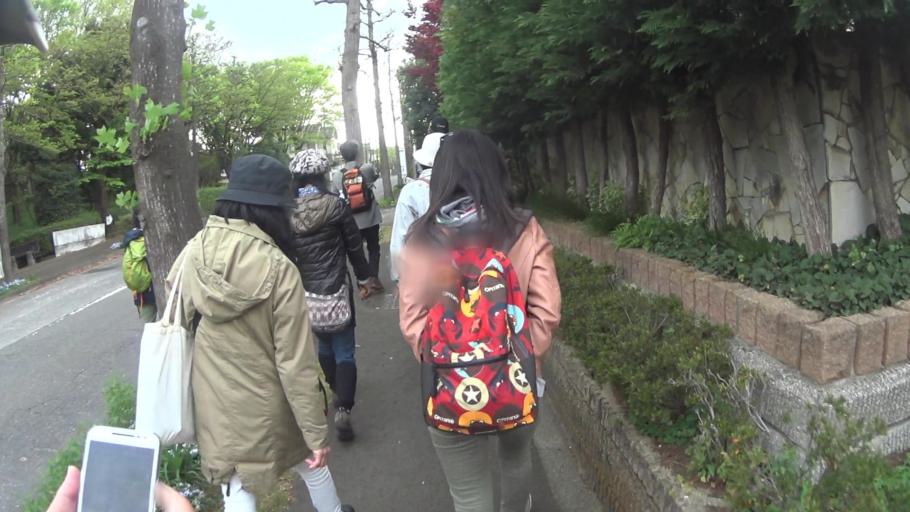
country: JP
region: Tokyo
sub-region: Machida-shi
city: Machida
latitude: 35.5697
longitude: 139.4856
